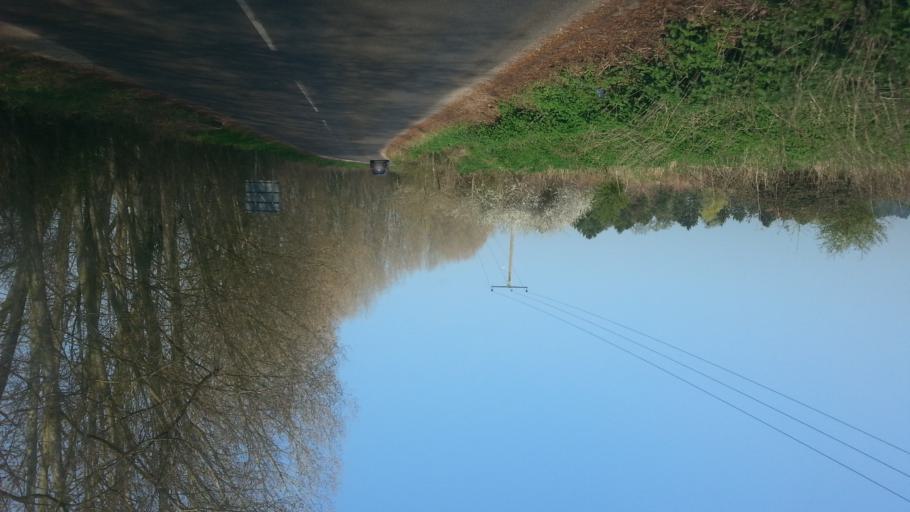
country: GB
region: England
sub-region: Suffolk
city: Thurston
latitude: 52.2388
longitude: 0.8272
